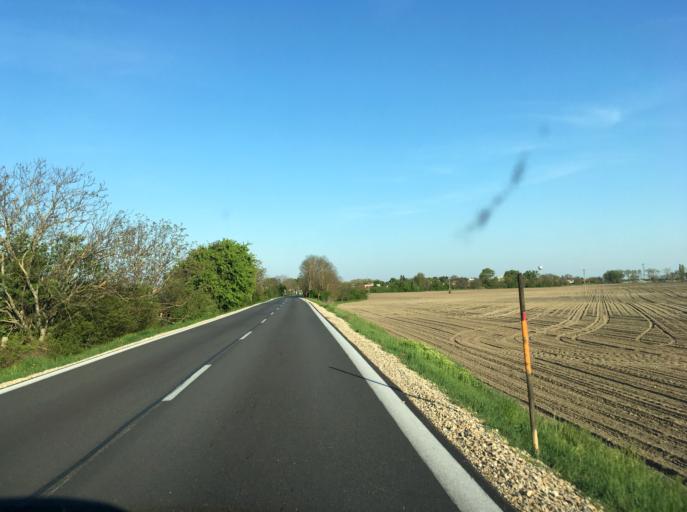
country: AT
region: Burgenland
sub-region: Politischer Bezirk Neusiedl am See
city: Deutsch Jahrndorf
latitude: 48.0596
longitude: 17.1325
